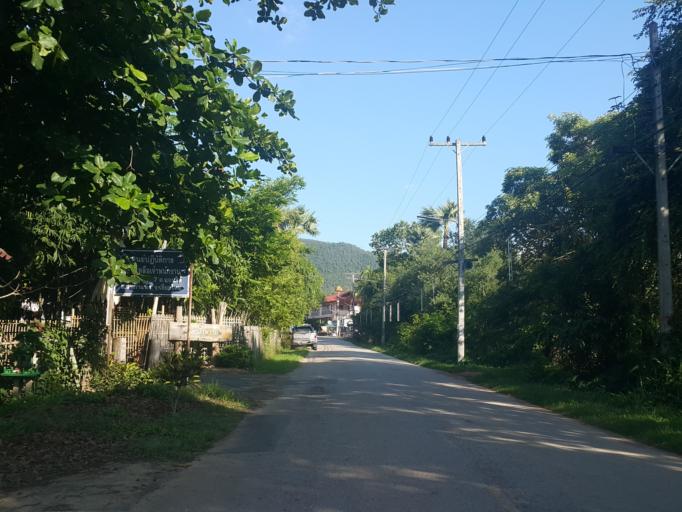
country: TH
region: Chiang Mai
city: Mae On
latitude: 18.7218
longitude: 99.2074
